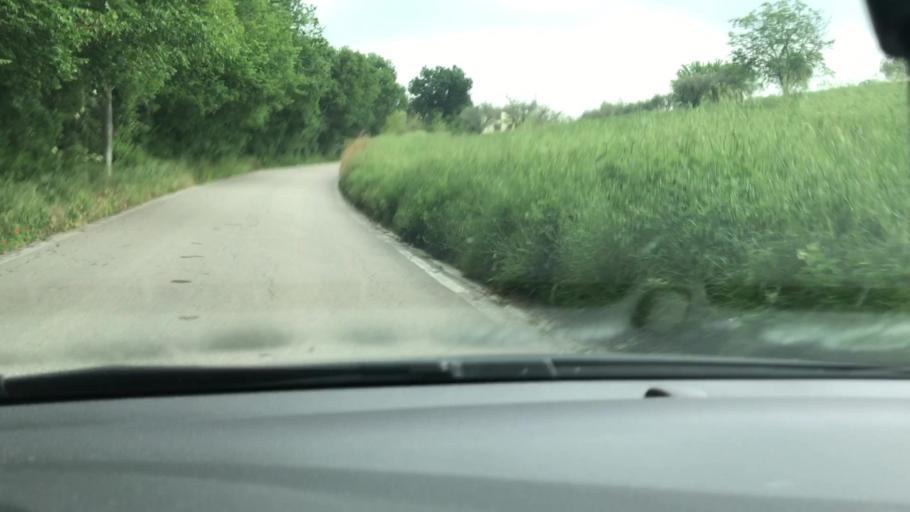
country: IT
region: The Marches
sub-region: Provincia di Macerata
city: Macerata
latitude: 43.2736
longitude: 13.4498
